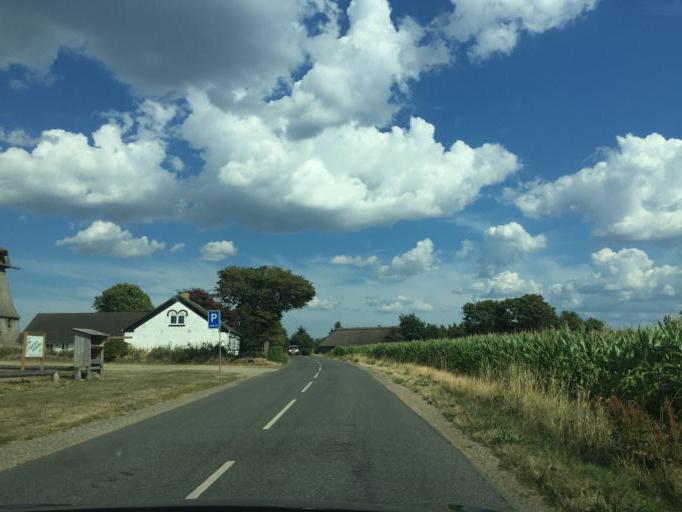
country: DK
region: South Denmark
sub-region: Assens Kommune
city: Harby
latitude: 55.1530
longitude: 10.0132
